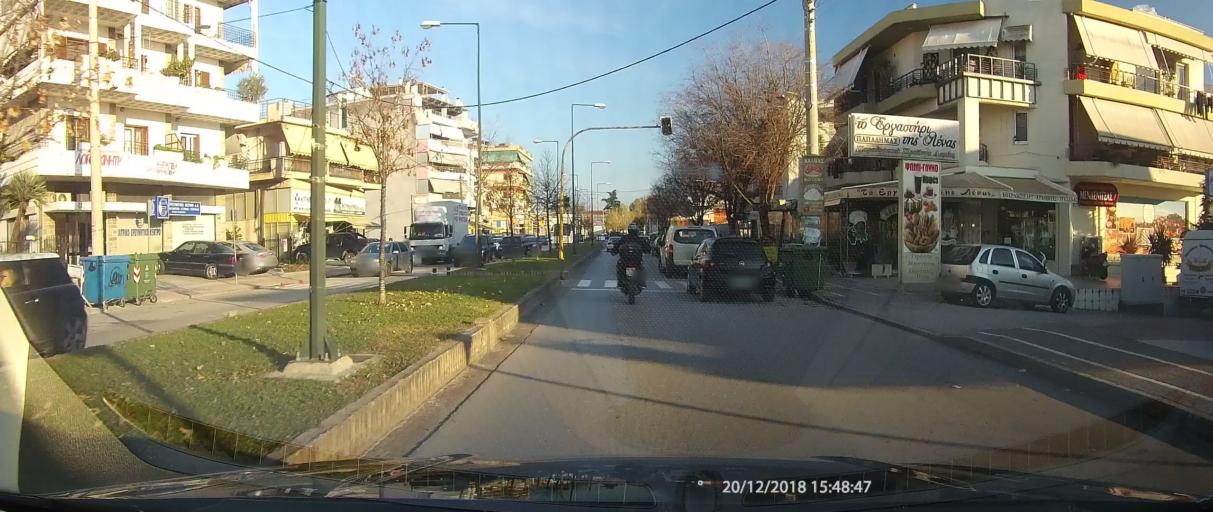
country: GR
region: Central Greece
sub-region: Nomos Fthiotidos
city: Lamia
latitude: 38.8943
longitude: 22.4423
